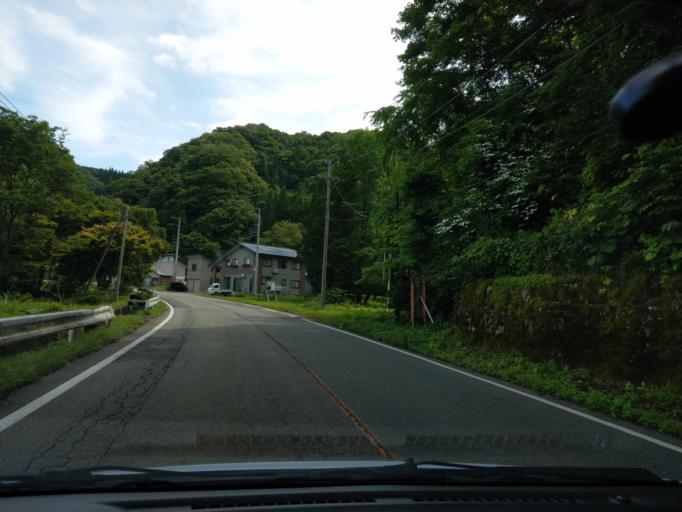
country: JP
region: Akita
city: Kakunodatemachi
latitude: 39.7493
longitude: 140.6014
